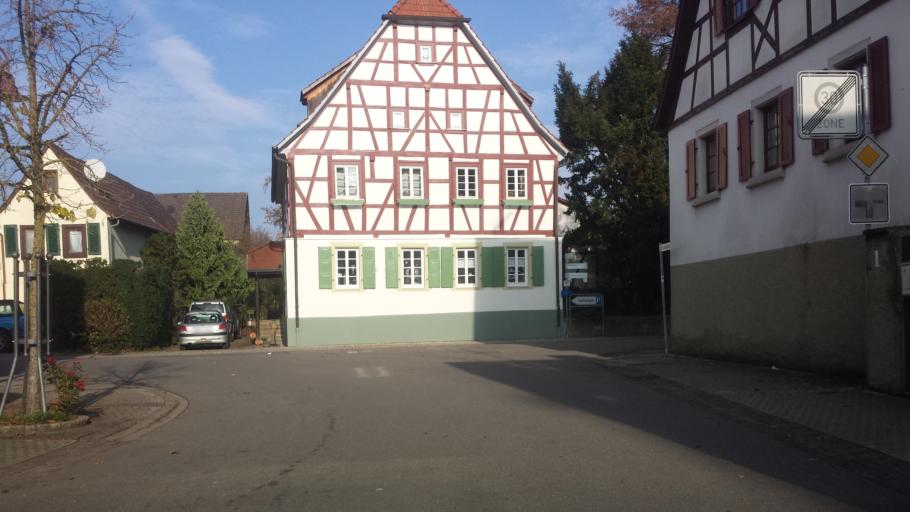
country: DE
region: Baden-Wuerttemberg
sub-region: Karlsruhe Region
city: Neckarbischofsheim
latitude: 49.3257
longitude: 8.9761
